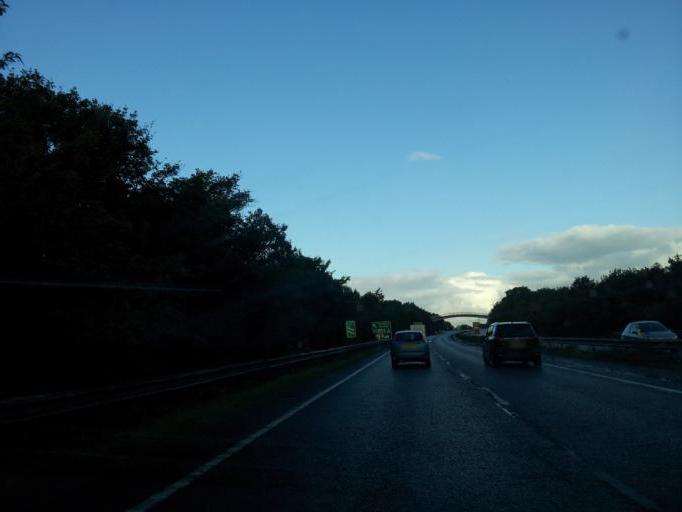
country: GB
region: England
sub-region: Norfolk
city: Cringleford
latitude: 52.5978
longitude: 1.2319
